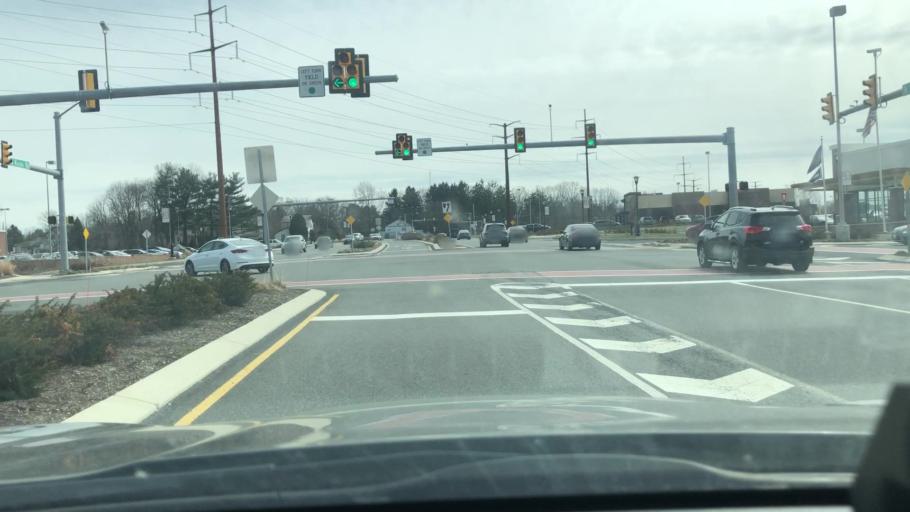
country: US
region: Pennsylvania
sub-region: Lehigh County
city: Wescosville
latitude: 40.5648
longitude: -75.5640
